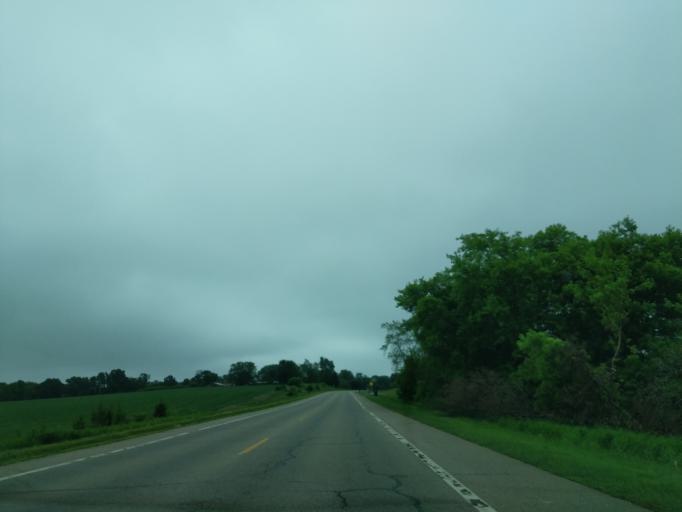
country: US
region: Michigan
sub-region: Hillsdale County
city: Litchfield
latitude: 42.0290
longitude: -84.7152
